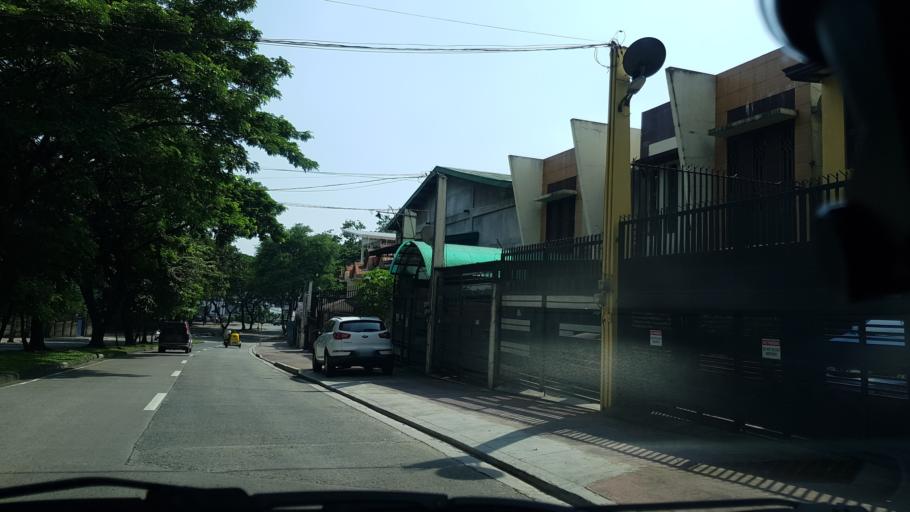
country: PH
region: Calabarzon
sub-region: Province of Rizal
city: Antipolo
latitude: 14.6522
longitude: 121.1159
